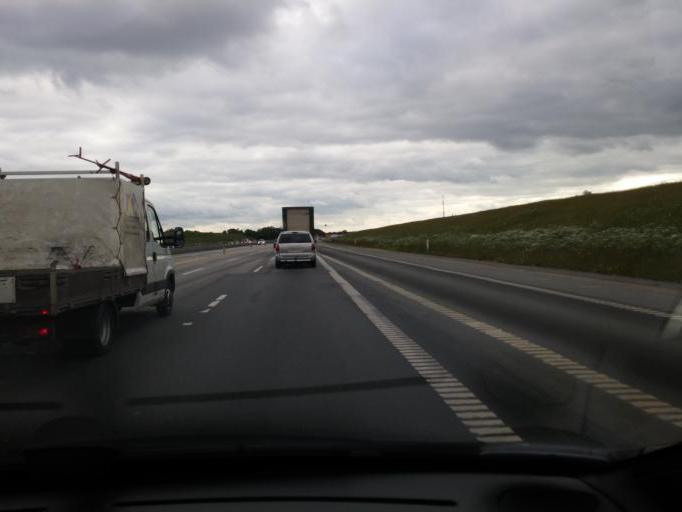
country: DK
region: Zealand
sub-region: Greve Kommune
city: Greve
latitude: 55.5796
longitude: 12.2554
